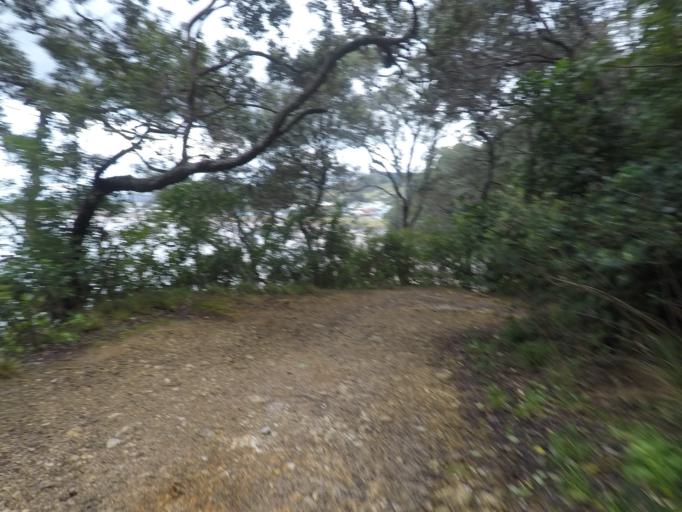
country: NZ
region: Bay of Plenty
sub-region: Western Bay of Plenty District
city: Waihi Beach
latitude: -37.3937
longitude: 175.9398
